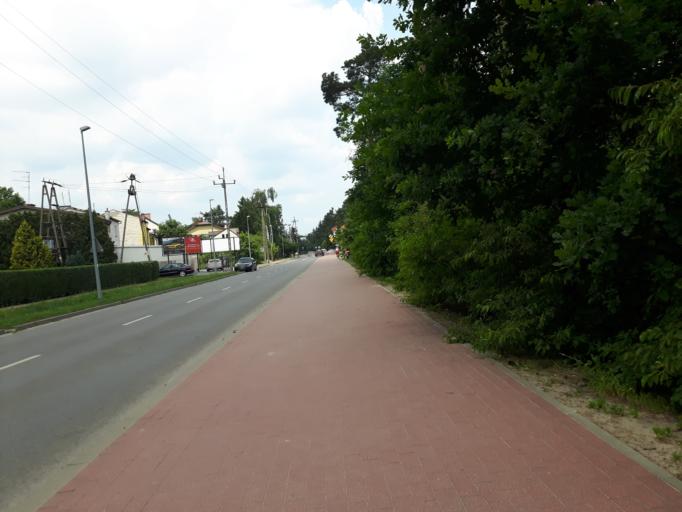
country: PL
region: Masovian Voivodeship
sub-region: Powiat wolominski
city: Zabki
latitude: 52.2890
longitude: 21.1260
